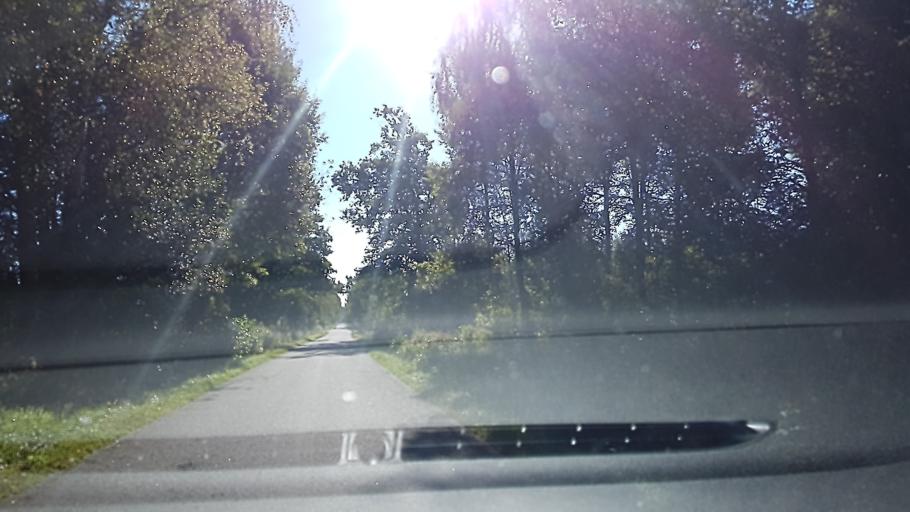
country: SE
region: Kronoberg
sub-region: Ljungby Kommun
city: Ljungby
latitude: 56.8089
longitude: 14.0211
